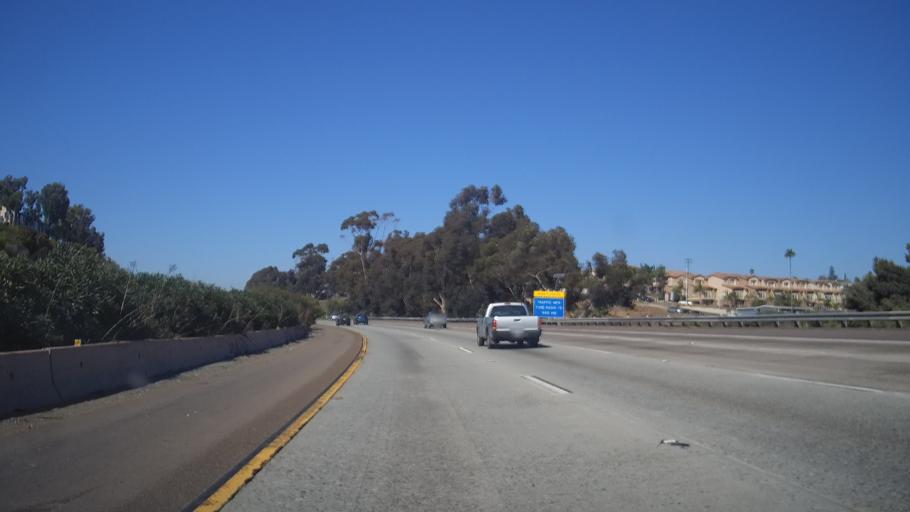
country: US
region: California
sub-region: San Diego County
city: Carlsbad
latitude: 33.1467
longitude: -117.3345
